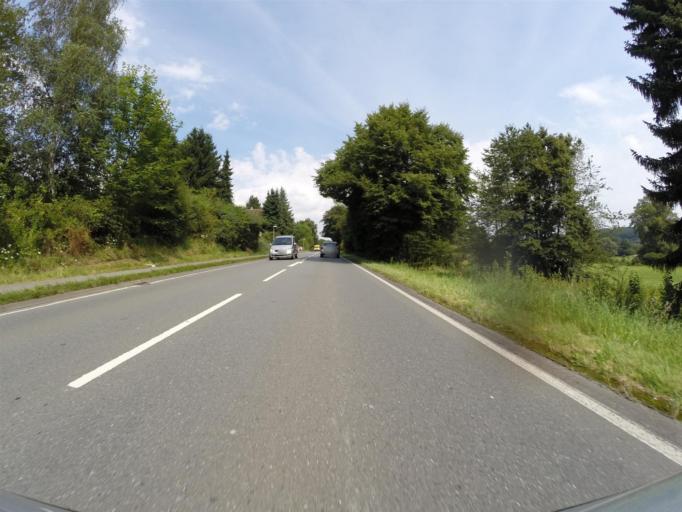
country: DE
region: North Rhine-Westphalia
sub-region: Regierungsbezirk Detmold
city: Herford
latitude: 52.1498
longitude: 8.6715
